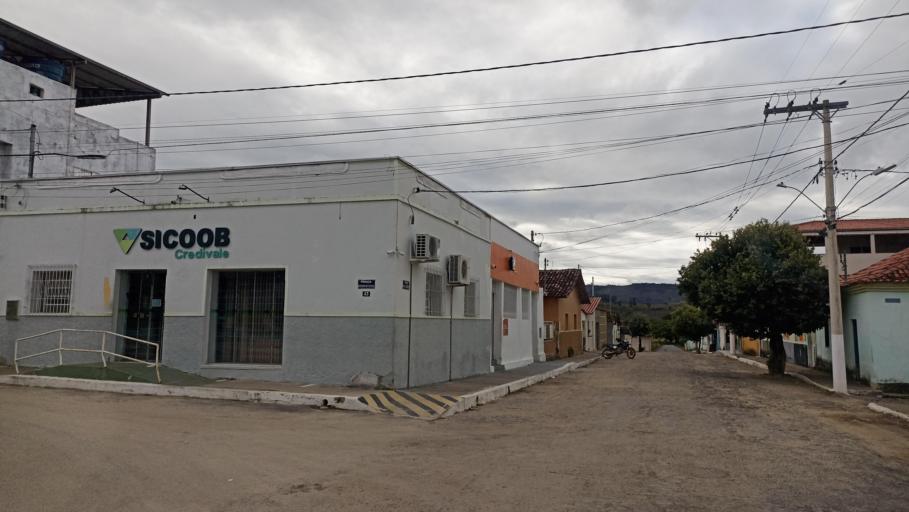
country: BR
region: Minas Gerais
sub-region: Almenara
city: Almenara
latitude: -16.6085
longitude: -40.5695
